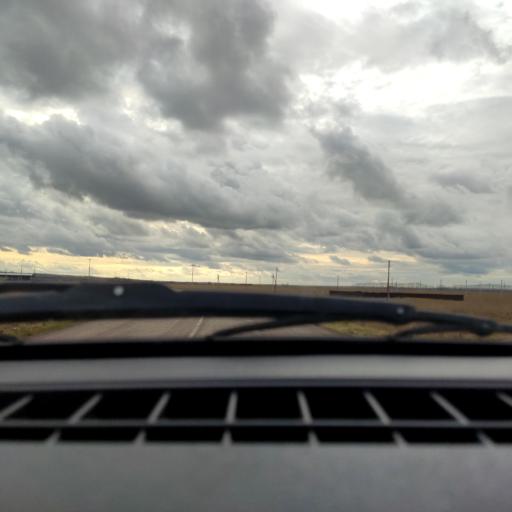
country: RU
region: Bashkortostan
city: Asanovo
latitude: 54.9589
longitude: 55.5356
